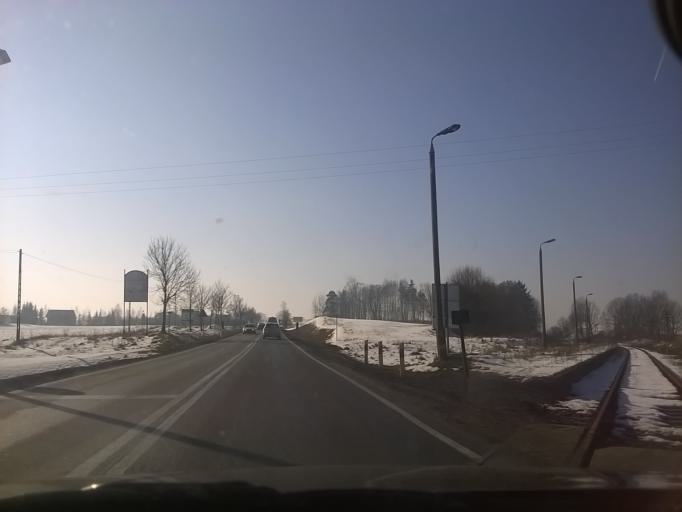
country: PL
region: Warmian-Masurian Voivodeship
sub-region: Powiat mragowski
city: Mragowo
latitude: 53.8509
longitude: 21.2361
